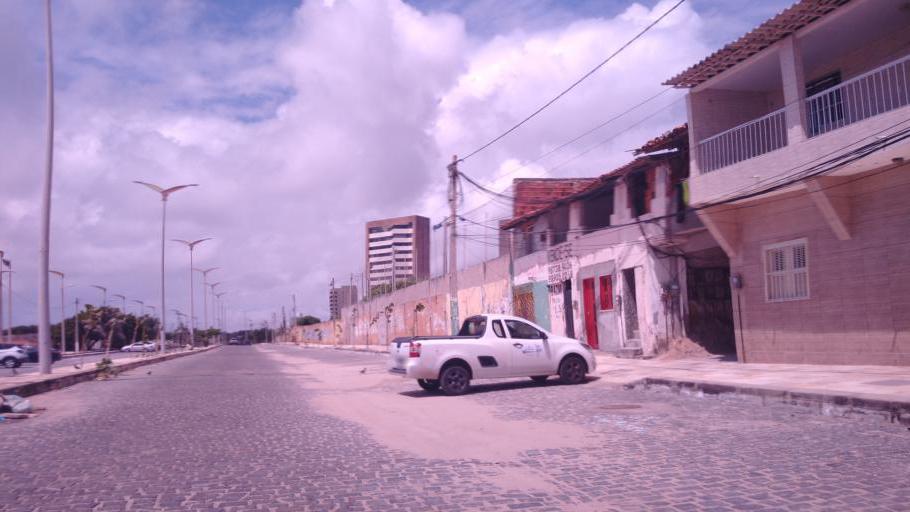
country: BR
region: Ceara
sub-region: Fortaleza
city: Fortaleza
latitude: -3.7284
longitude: -38.4591
